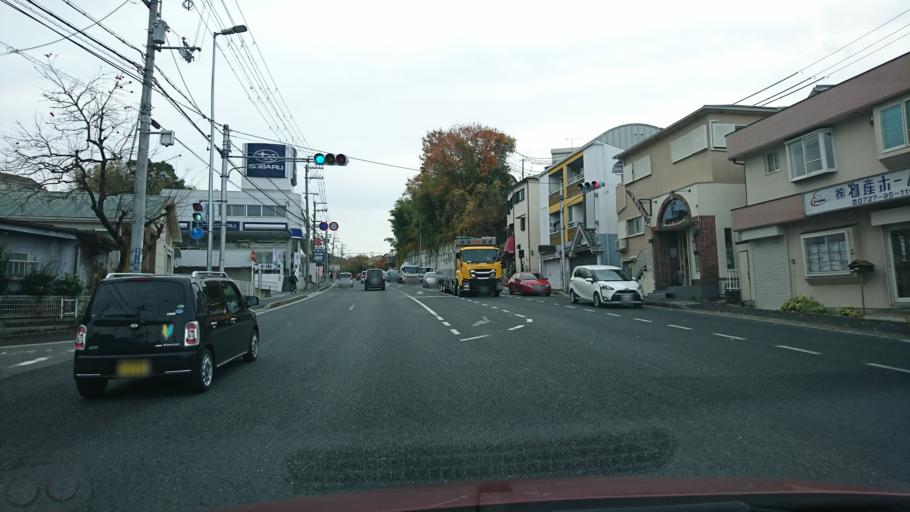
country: JP
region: Osaka
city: Ikeda
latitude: 34.8836
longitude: 135.4153
